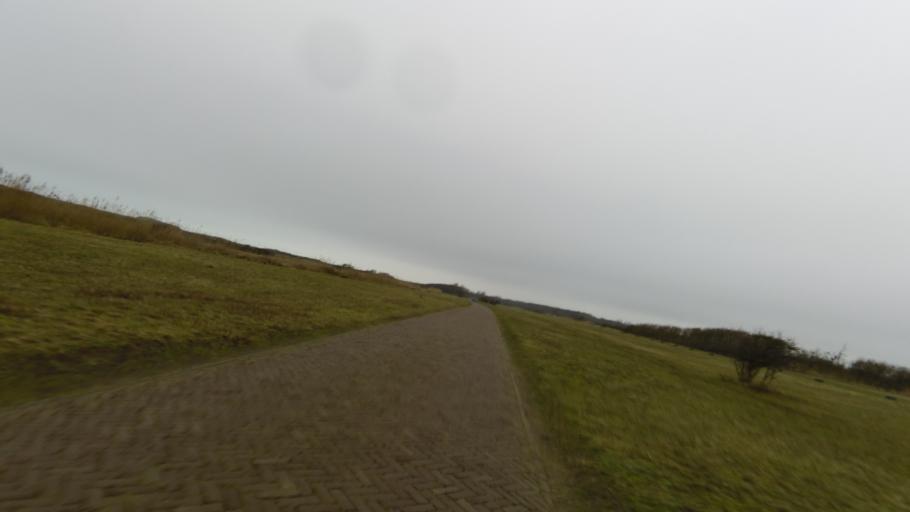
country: NL
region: North Holland
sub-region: Gemeente Castricum
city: Castricum
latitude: 52.5451
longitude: 4.6182
